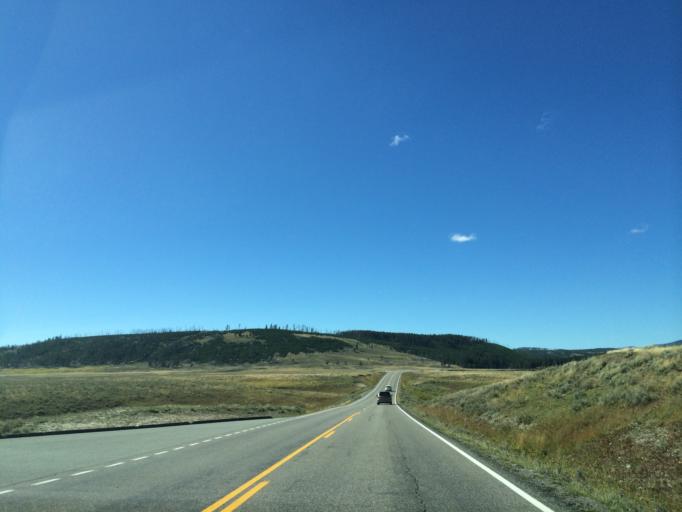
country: US
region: Montana
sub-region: Gallatin County
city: West Yellowstone
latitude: 44.6732
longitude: -110.4781
